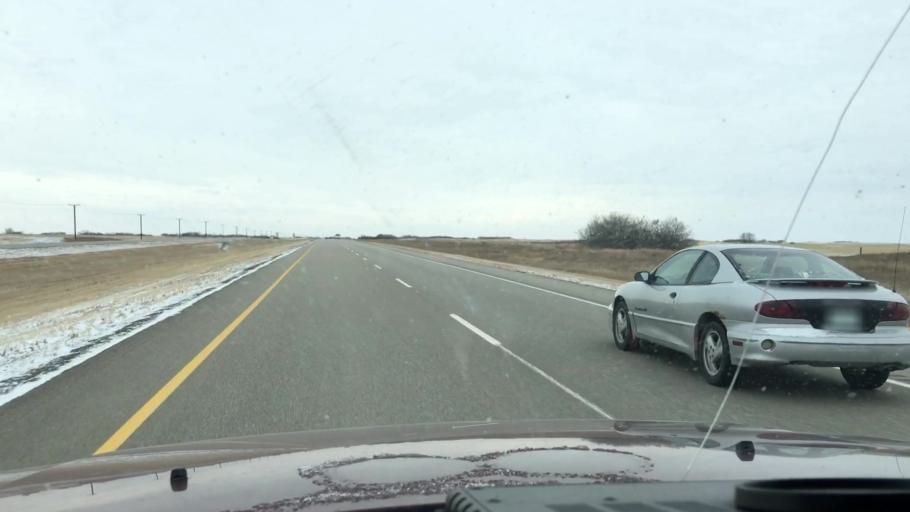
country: CA
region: Saskatchewan
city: Watrous
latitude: 51.4050
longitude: -106.1807
